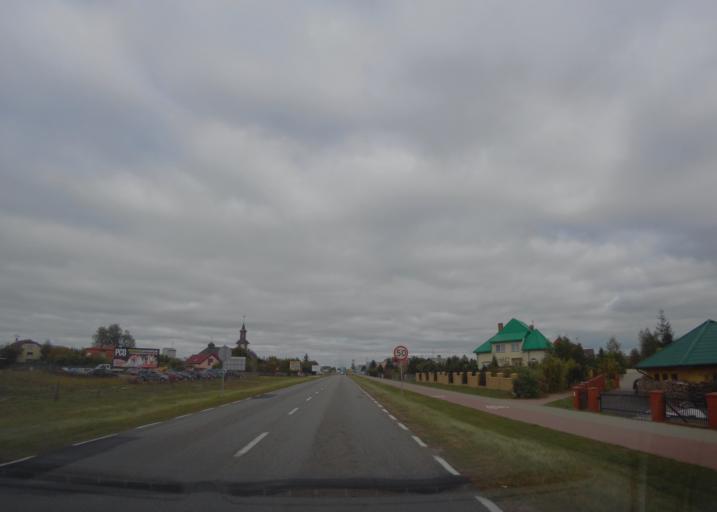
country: PL
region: Lublin Voivodeship
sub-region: Powiat wlodawski
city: Wlodawa
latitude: 51.5436
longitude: 23.5404
